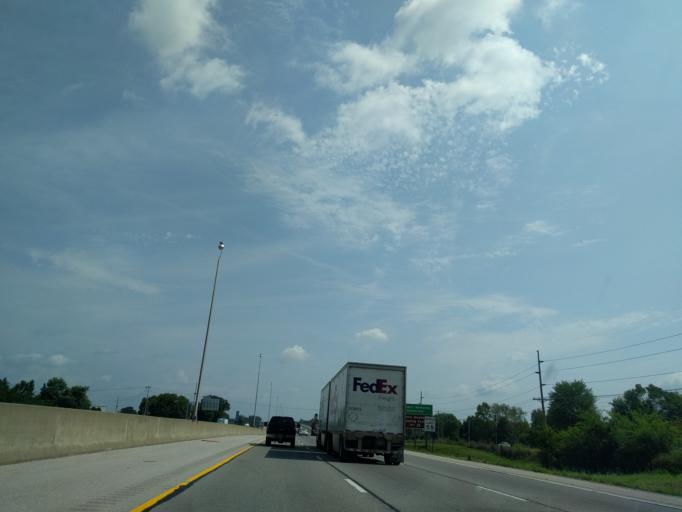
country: US
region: Kentucky
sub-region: Warren County
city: Bowling Green
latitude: 36.9496
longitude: -86.4090
